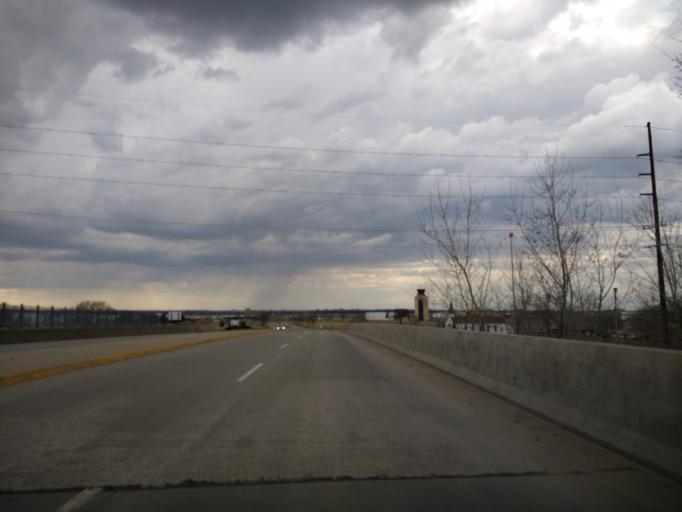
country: US
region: Iowa
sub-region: Woodbury County
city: Sergeant Bluff
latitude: 42.4008
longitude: -96.3694
